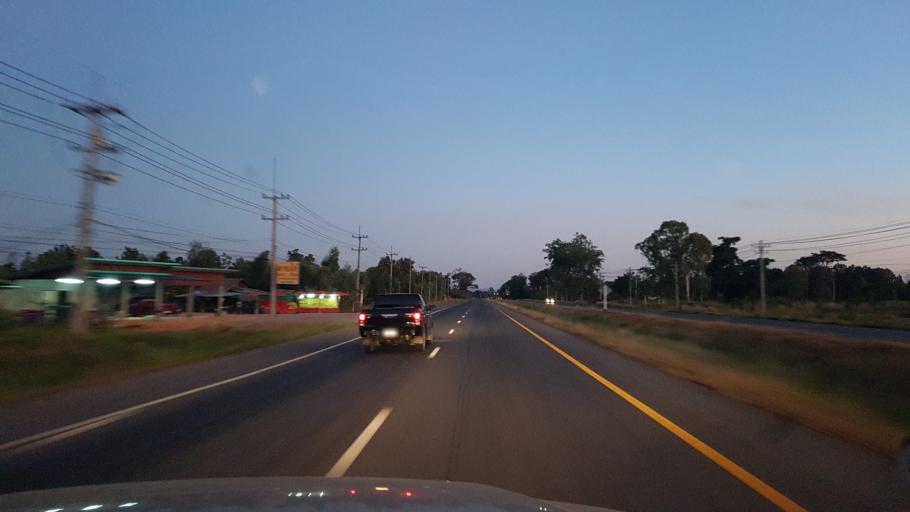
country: TH
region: Chaiyaphum
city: Phu Khiao
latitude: 16.3115
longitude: 102.2012
